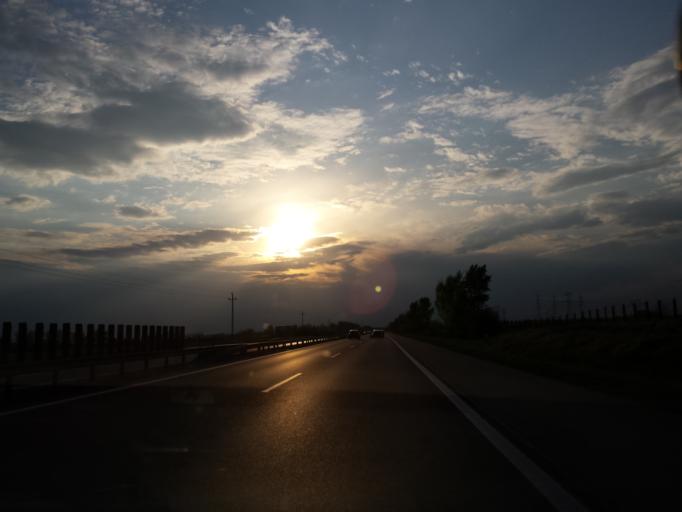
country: HU
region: Gyor-Moson-Sopron
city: Gyorujbarat
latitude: 47.6362
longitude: 17.6519
